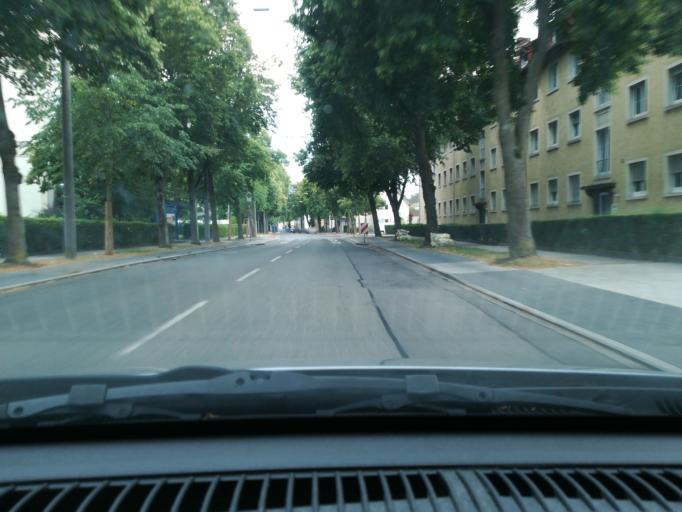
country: DE
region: Baden-Wuerttemberg
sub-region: Freiburg Region
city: Singen
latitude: 47.7495
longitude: 8.8428
